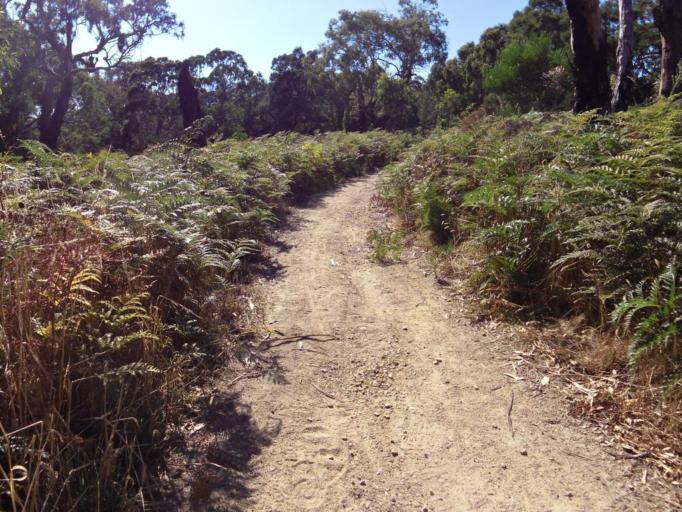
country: AU
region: Victoria
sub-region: Mornington Peninsula
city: Mount Martha
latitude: -38.2629
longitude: 145.0439
